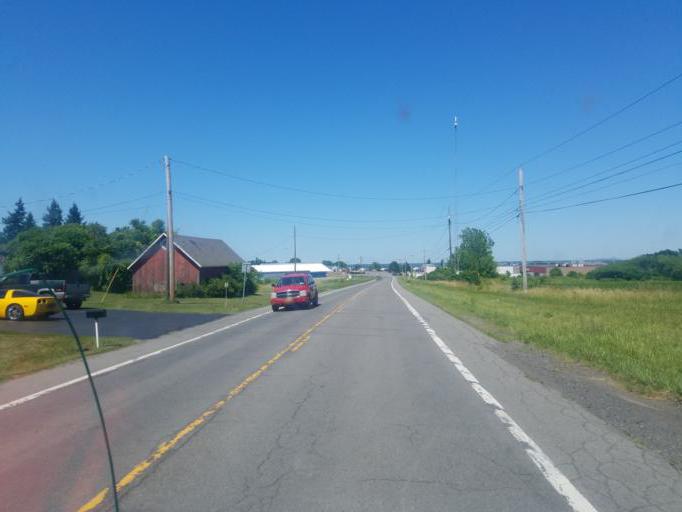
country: US
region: New York
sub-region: Ontario County
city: Geneva
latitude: 42.8513
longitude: -77.0169
